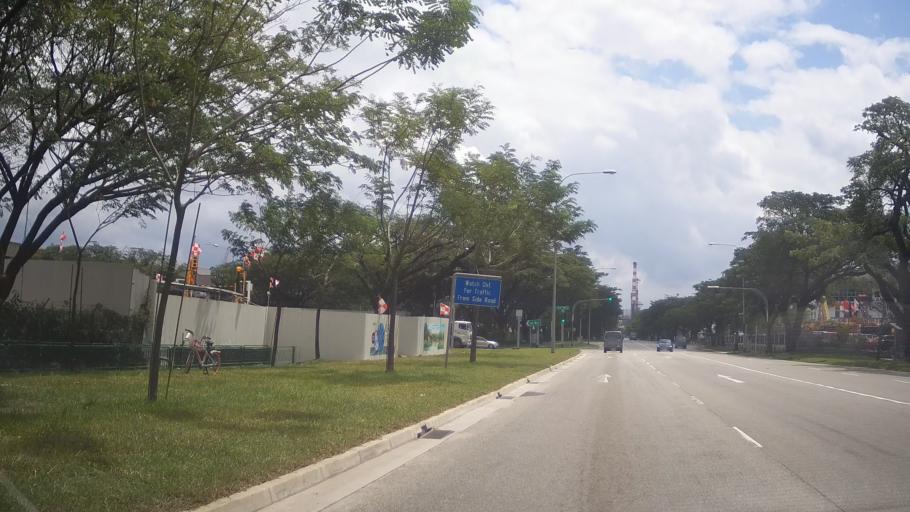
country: MY
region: Johor
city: Johor Bahru
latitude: 1.3087
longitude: 103.6703
